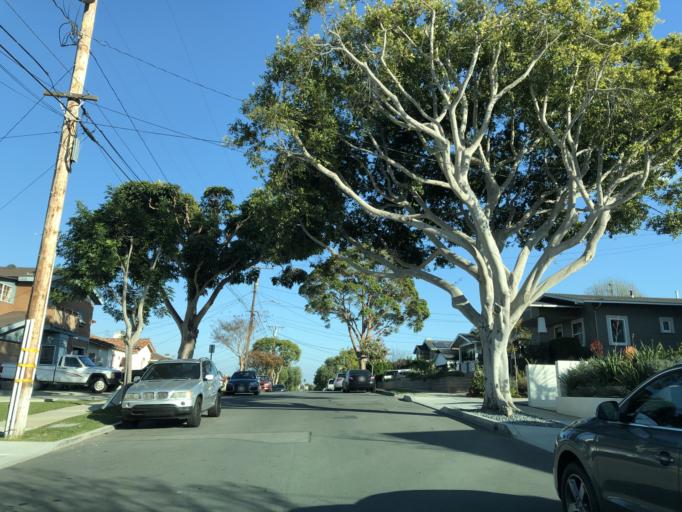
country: US
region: California
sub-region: Los Angeles County
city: El Segundo
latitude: 33.9260
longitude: -118.4184
